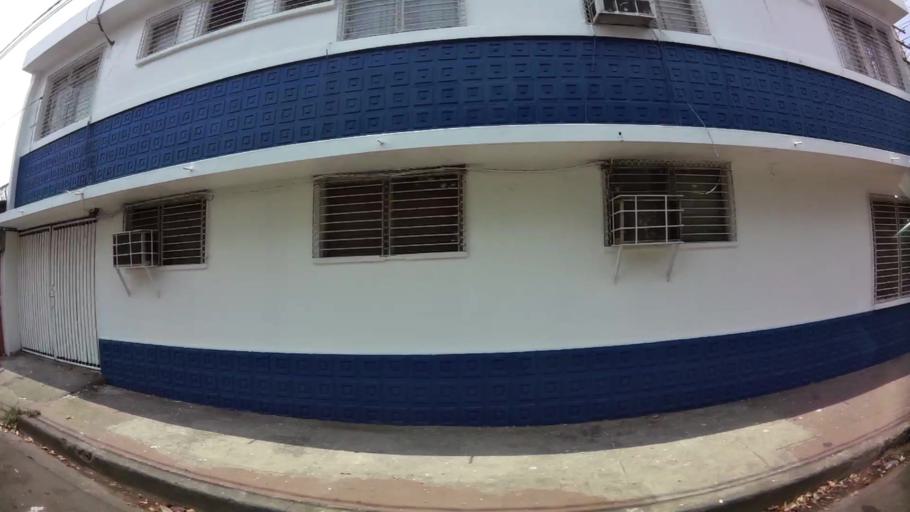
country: NI
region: Managua
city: Managua
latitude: 12.1487
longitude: -86.2879
